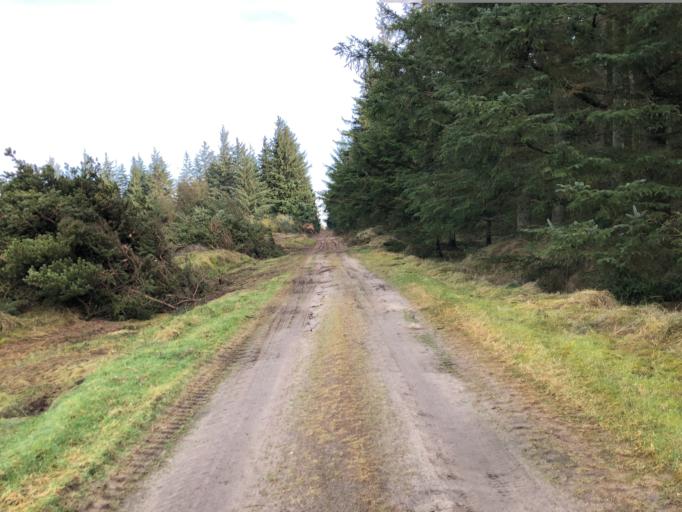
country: DK
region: Central Jutland
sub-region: Holstebro Kommune
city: Ulfborg
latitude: 56.2572
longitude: 8.3688
